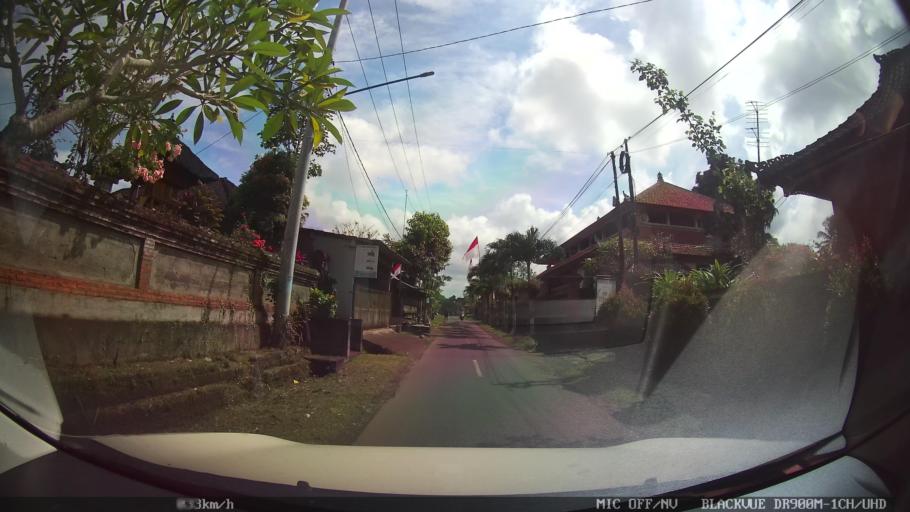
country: ID
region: Bali
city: Banjar Tebongkang
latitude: -8.5369
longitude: 115.2521
